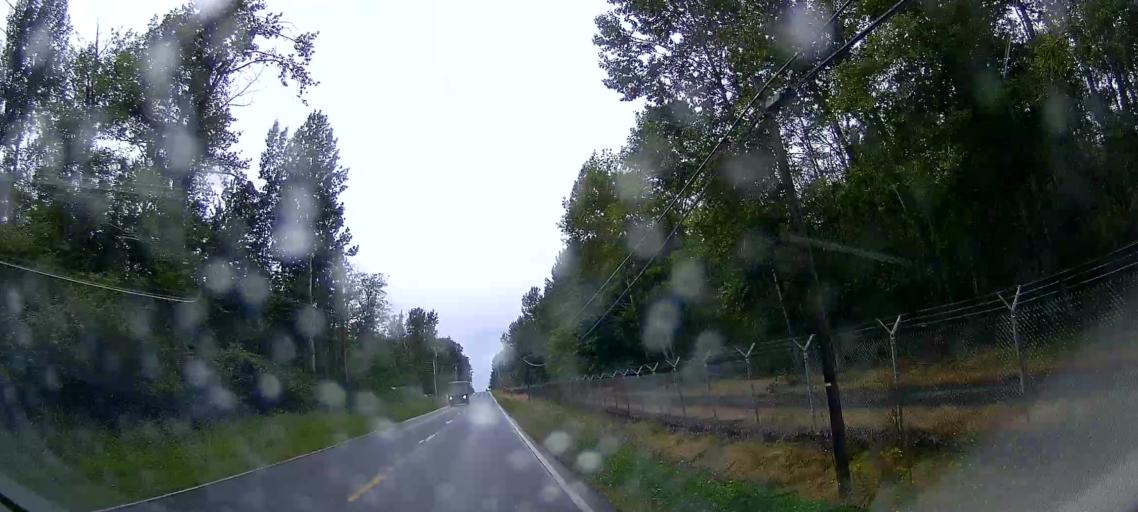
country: US
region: Washington
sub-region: Whatcom County
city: Ferndale
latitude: 48.8195
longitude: -122.6902
